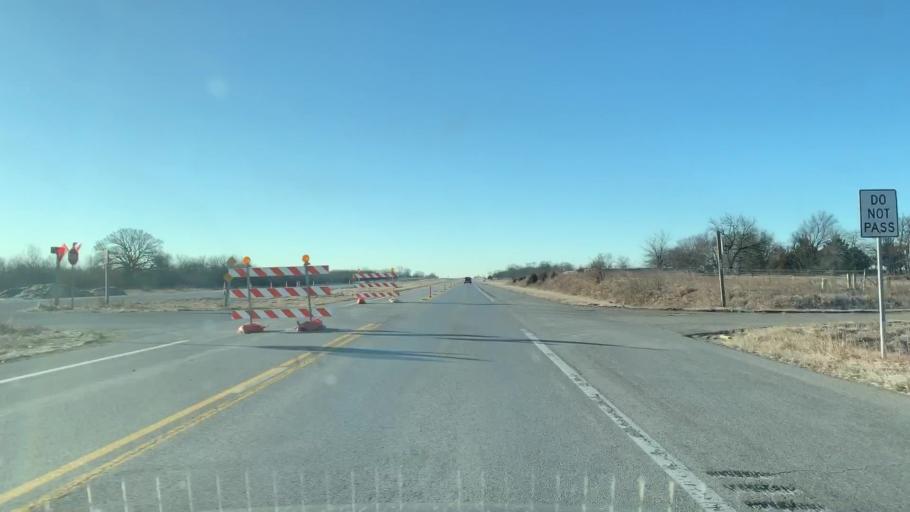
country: US
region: Kansas
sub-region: Bourbon County
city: Fort Scott
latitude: 37.7616
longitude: -94.7050
